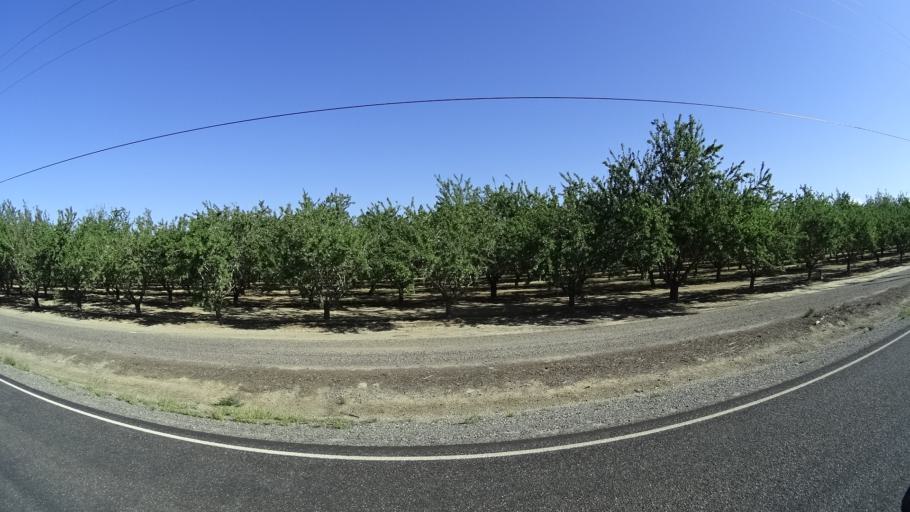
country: US
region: California
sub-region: Glenn County
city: Hamilton City
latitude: 39.7092
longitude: -122.0609
